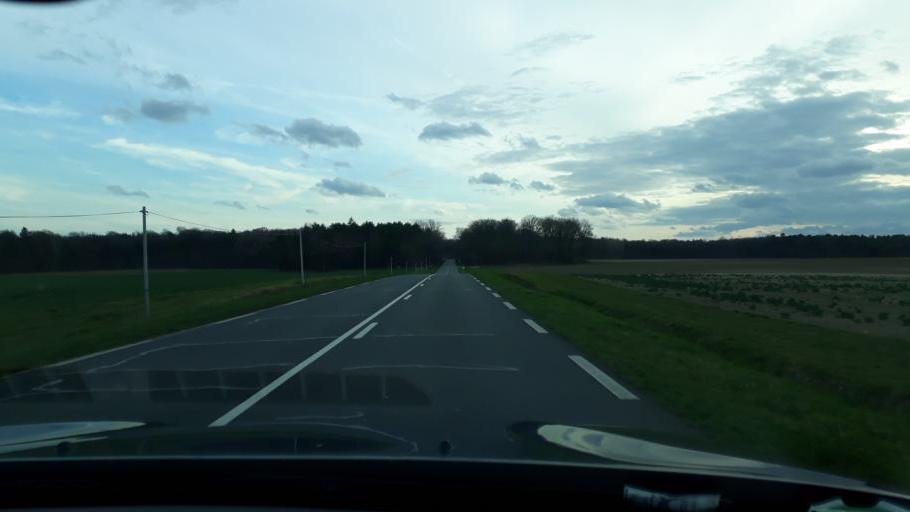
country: FR
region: Centre
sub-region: Departement du Loiret
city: Chilleurs-aux-Bois
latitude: 48.0591
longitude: 2.1294
